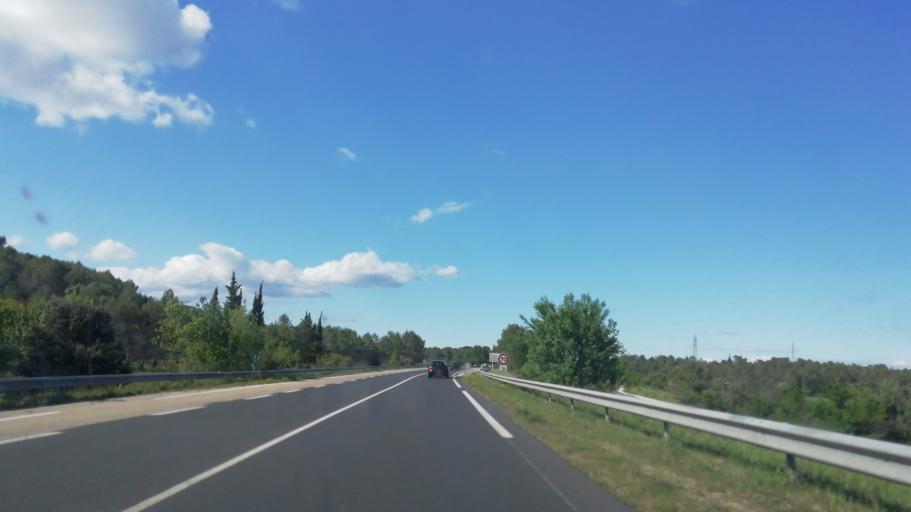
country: FR
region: Languedoc-Roussillon
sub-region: Departement de l'Herault
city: Saint-Clement-de-Riviere
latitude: 43.6848
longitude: 3.8220
